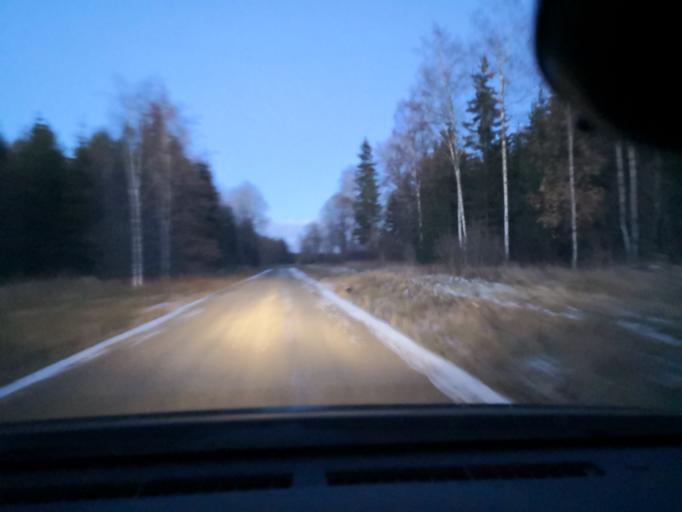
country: SE
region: Vaestmanland
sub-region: Sala Kommun
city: Sala
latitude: 59.8694
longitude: 16.6824
